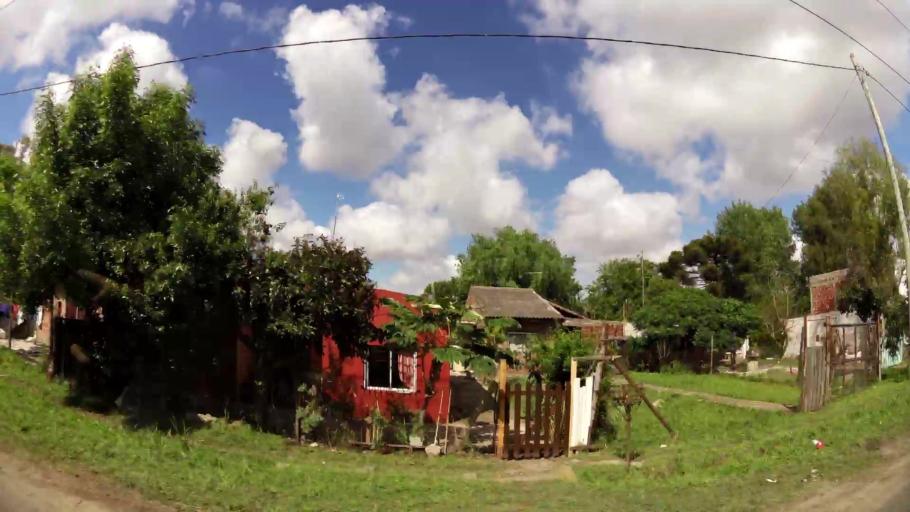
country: AR
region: Buenos Aires
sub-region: Partido de Quilmes
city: Quilmes
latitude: -34.8329
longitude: -58.1723
